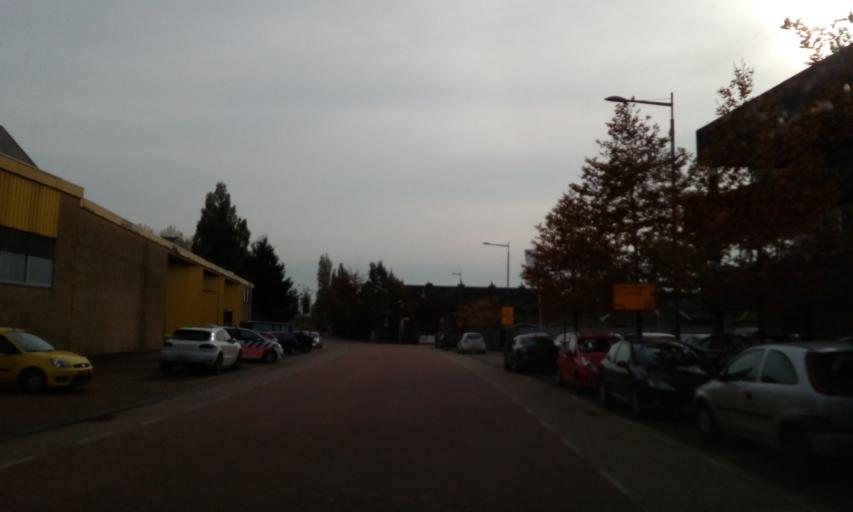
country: NL
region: South Holland
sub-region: Gemeente Lansingerland
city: Berkel en Rodenrijs
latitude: 51.9779
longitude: 4.4572
